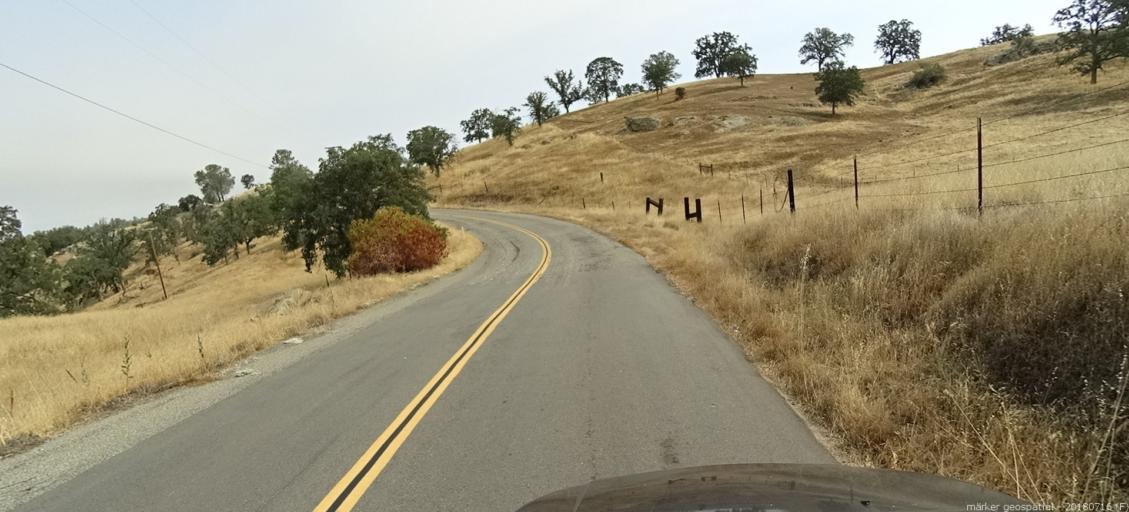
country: US
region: California
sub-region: Madera County
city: Yosemite Lakes
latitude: 37.1421
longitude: -119.8531
